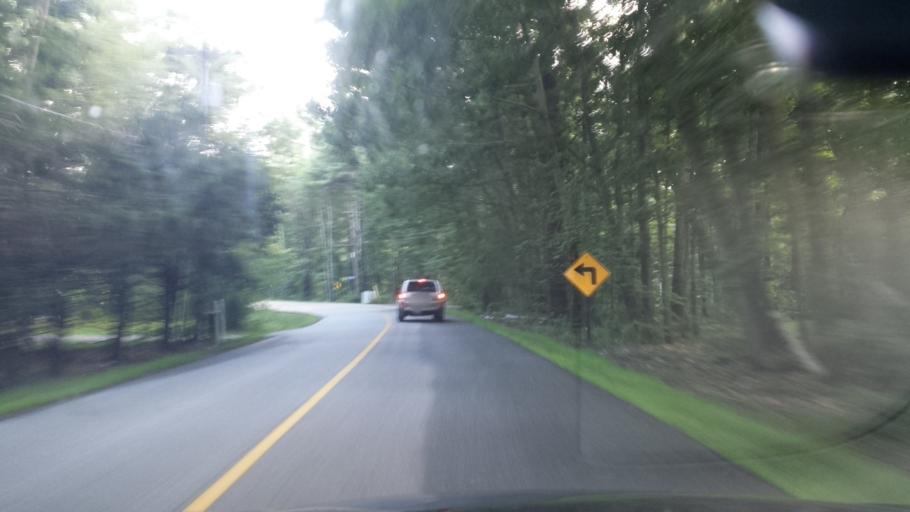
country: US
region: Maine
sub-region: York County
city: Arundel
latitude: 43.4312
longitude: -70.4551
